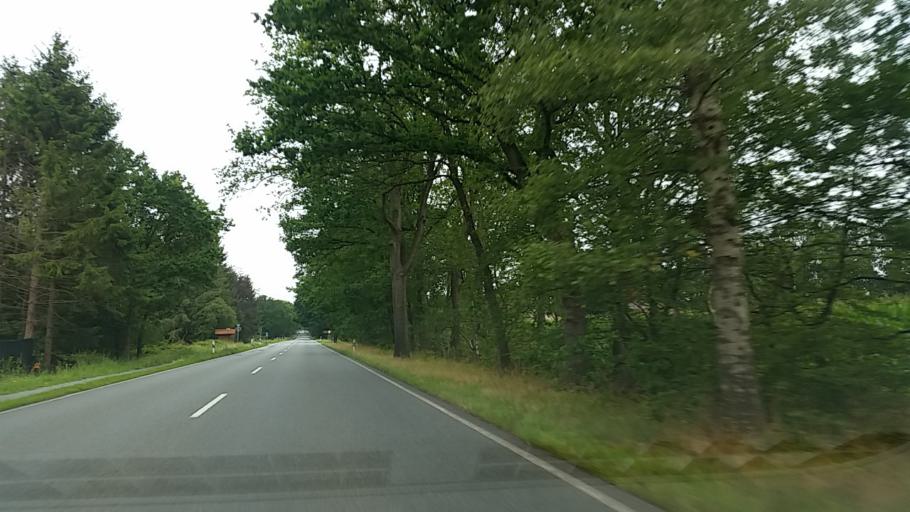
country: DE
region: Lower Saxony
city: Loxstedt
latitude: 53.4789
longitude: 8.7001
